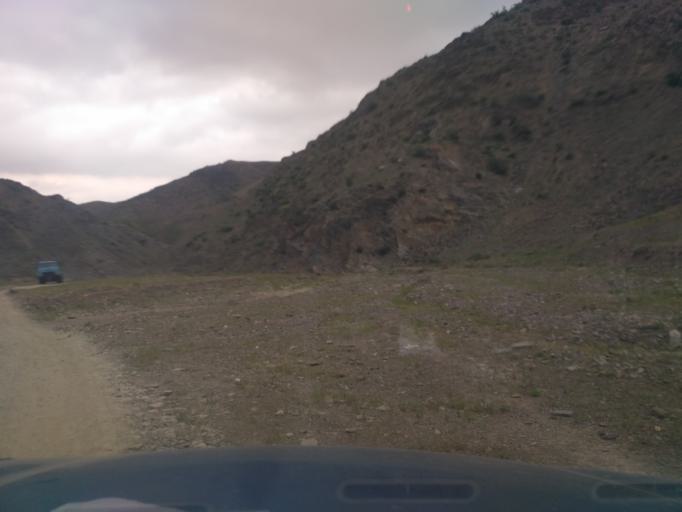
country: UZ
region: Jizzax
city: Zomin
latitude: 39.8503
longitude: 68.3964
